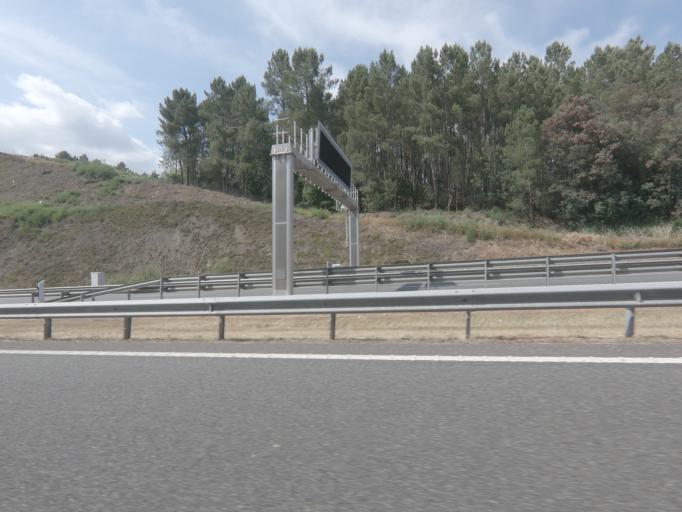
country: ES
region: Galicia
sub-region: Provincia de Ourense
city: Beade
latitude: 42.3080
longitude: -8.1078
